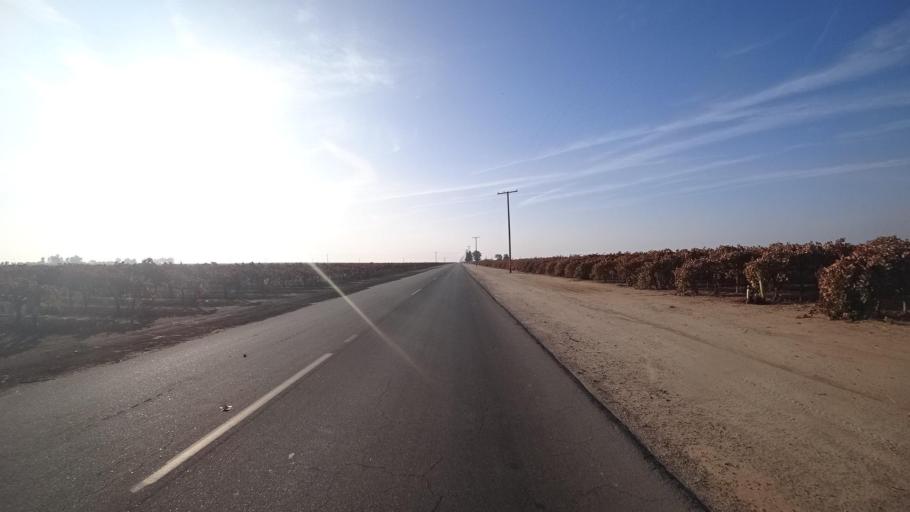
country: US
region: California
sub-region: Kern County
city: Delano
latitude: 35.7535
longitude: -119.1874
